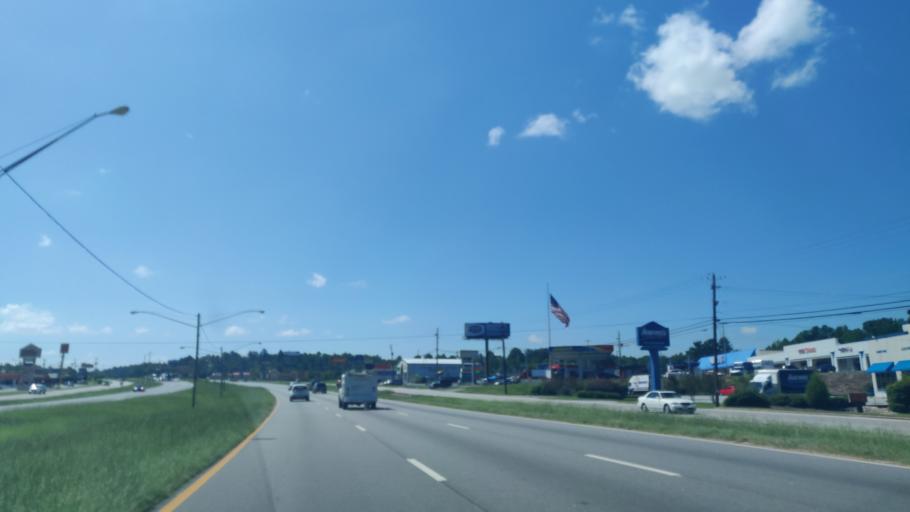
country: US
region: Alabama
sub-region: Russell County
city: Phenix City
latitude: 32.4693
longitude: -85.0290
